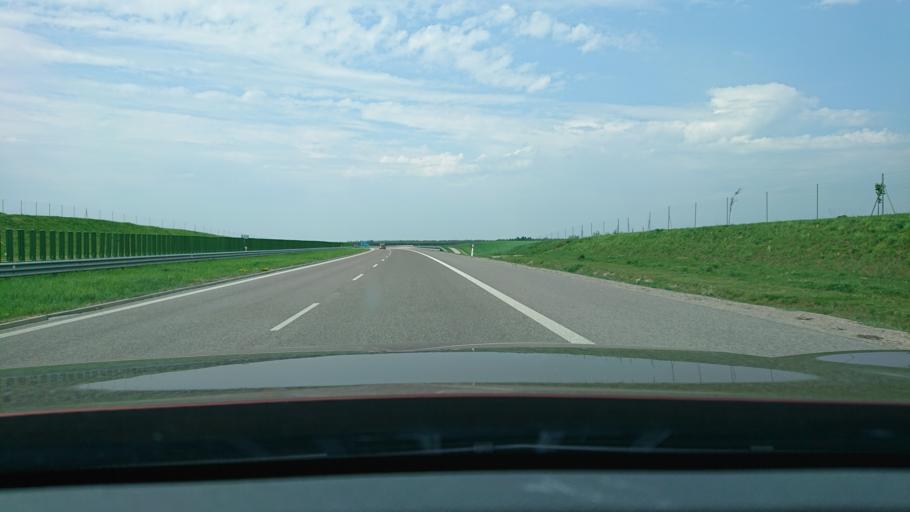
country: PL
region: Subcarpathian Voivodeship
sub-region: Powiat jaroslawski
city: Pawlosiow
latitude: 49.9612
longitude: 22.6586
